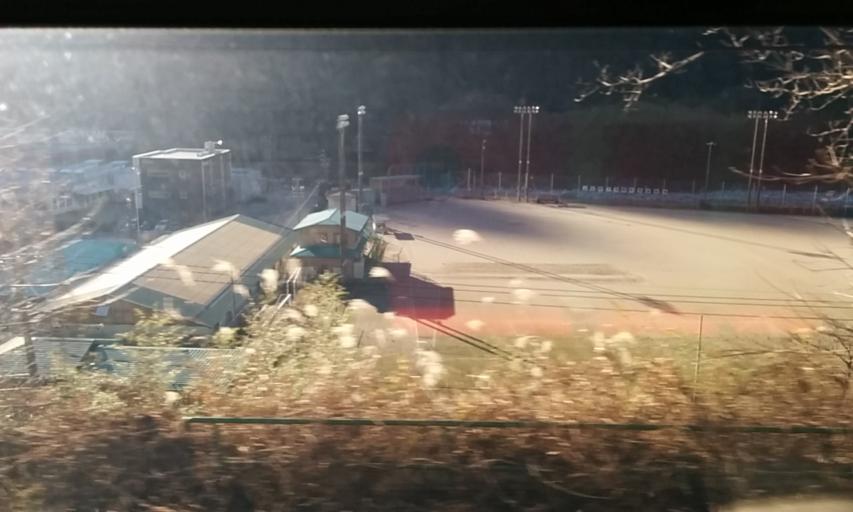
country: JP
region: Nagano
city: Iida
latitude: 35.7476
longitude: 137.7143
